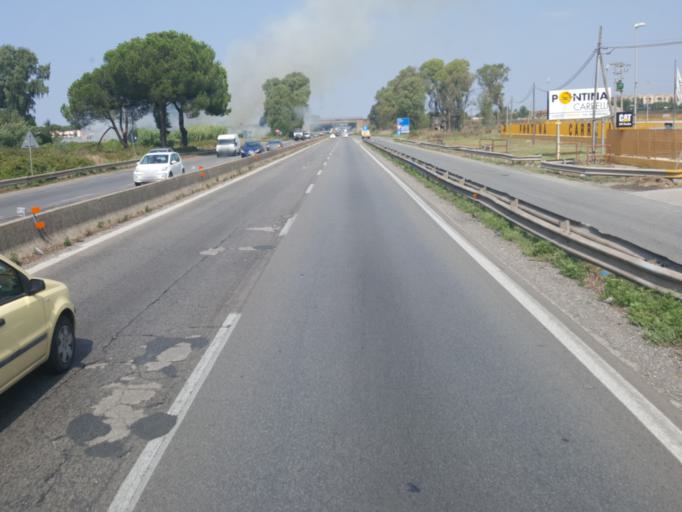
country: IT
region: Latium
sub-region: Provincia di Latina
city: Genio Civile
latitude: 41.5664
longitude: 12.6737
